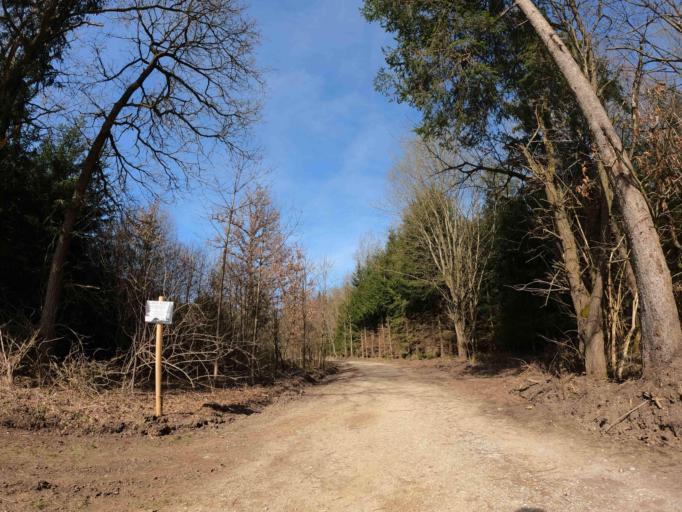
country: DE
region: Bavaria
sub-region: Upper Bavaria
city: Brunnthal
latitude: 47.9942
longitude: 11.7004
